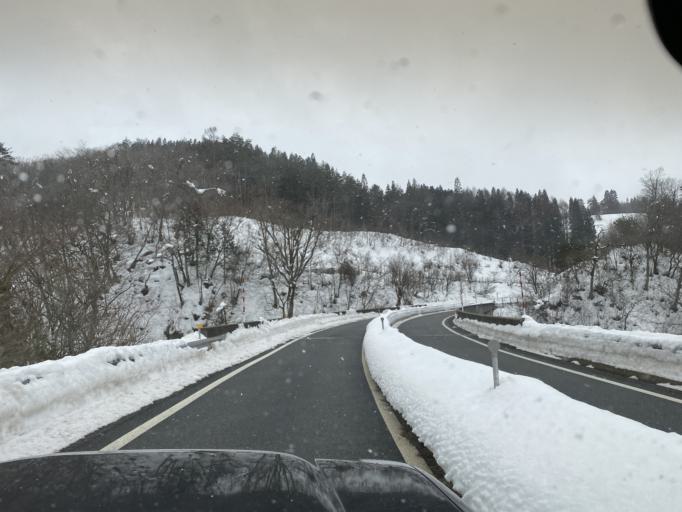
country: JP
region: Gifu
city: Gujo
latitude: 36.0203
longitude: 136.9660
